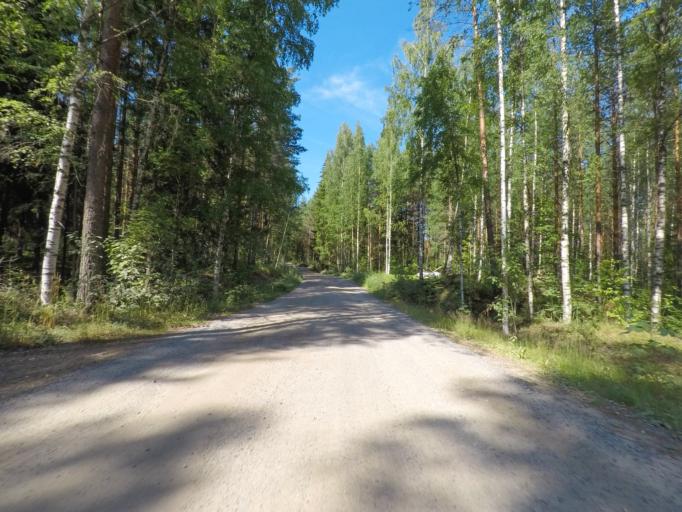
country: FI
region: Southern Savonia
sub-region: Mikkeli
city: Puumala
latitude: 61.4250
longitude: 28.0363
